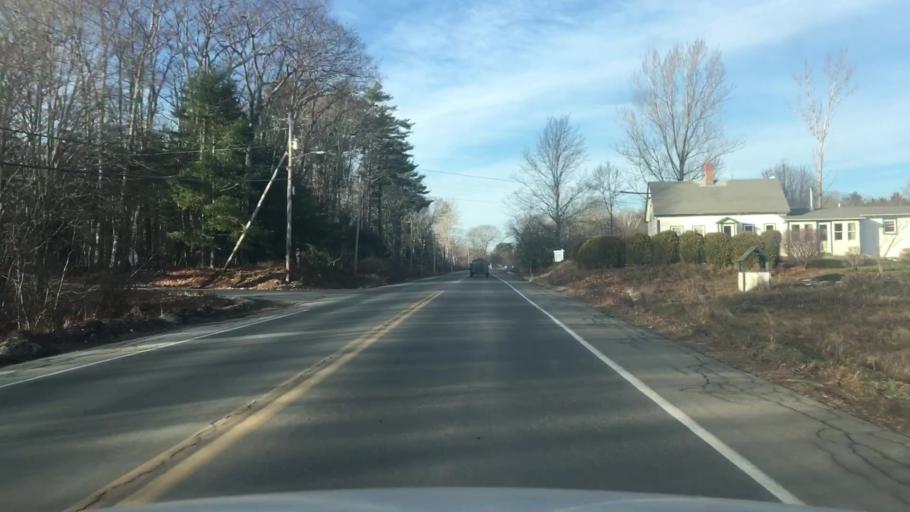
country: US
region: Maine
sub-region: Lincoln County
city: Wiscasset
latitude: 44.0295
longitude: -69.6720
